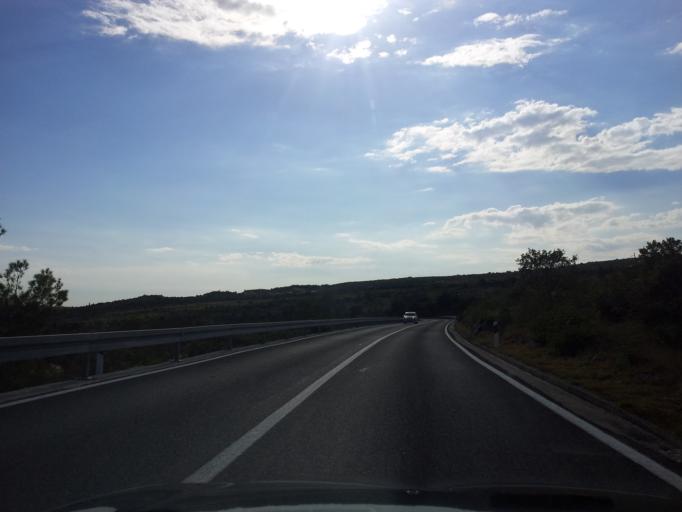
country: HR
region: Zadarska
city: Posedarje
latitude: 44.2226
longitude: 15.5197
